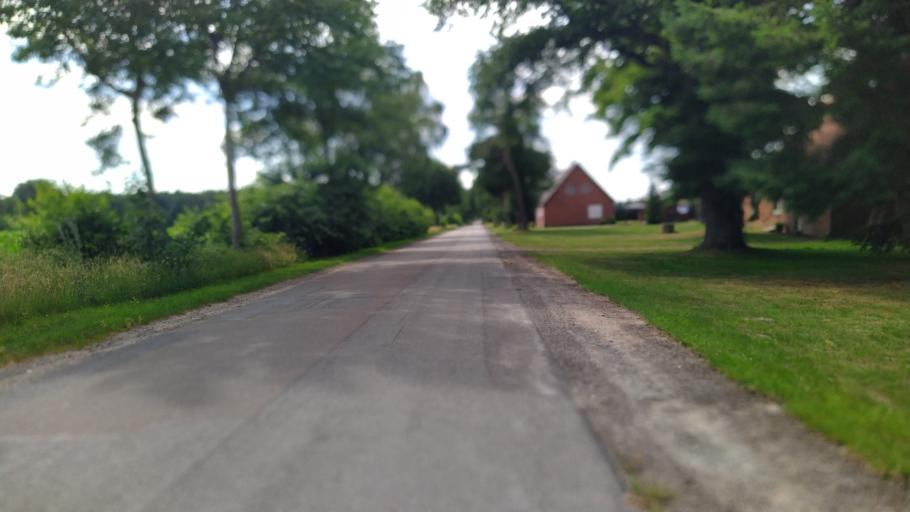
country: DE
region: Lower Saxony
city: Armstorf
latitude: 53.6063
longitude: 9.0546
